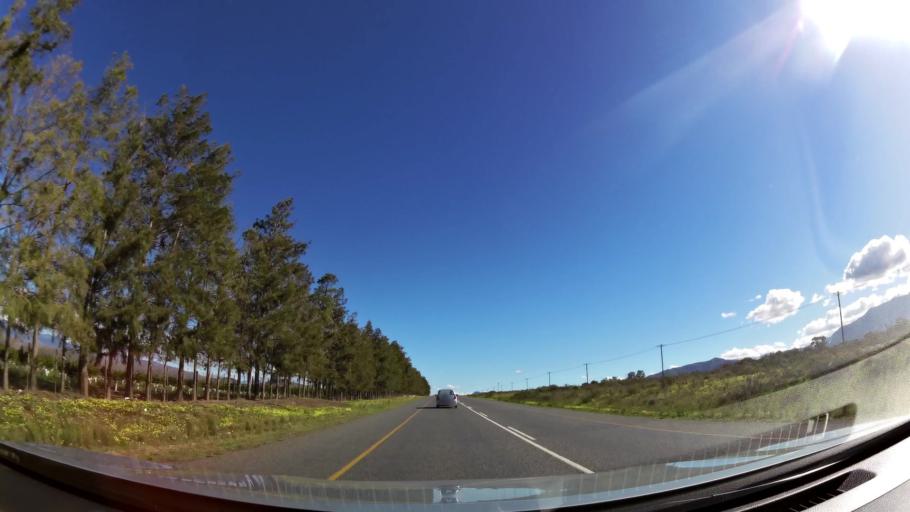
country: ZA
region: Western Cape
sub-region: Cape Winelands District Municipality
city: Ashton
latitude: -33.8144
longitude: 19.9267
